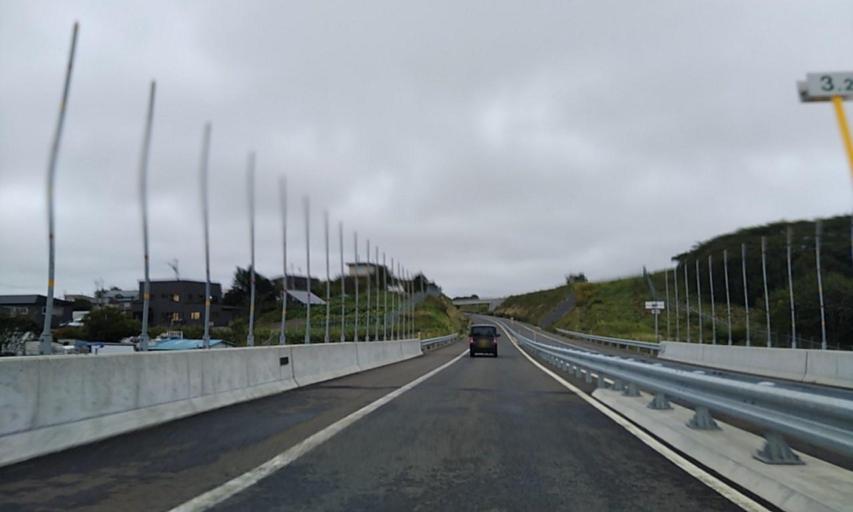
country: JP
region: Hokkaido
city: Nemuro
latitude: 43.2957
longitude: 145.5224
